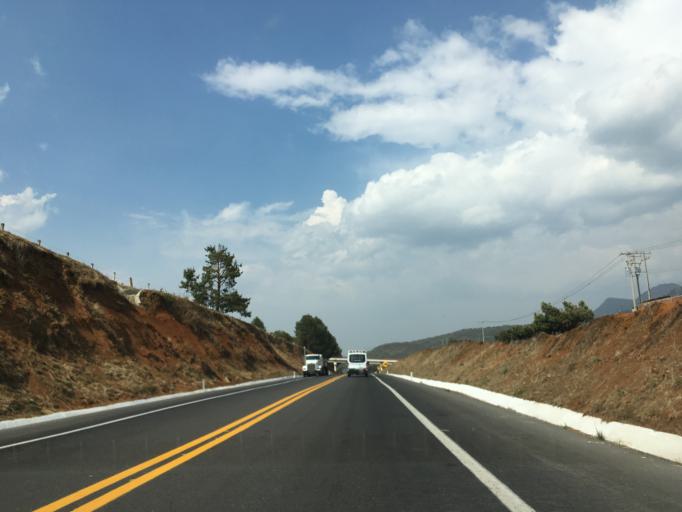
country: MX
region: Michoacan
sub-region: Patzcuaro
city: Colonia Vista Bella (Lomas del Peaje)
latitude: 19.5034
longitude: -101.5807
